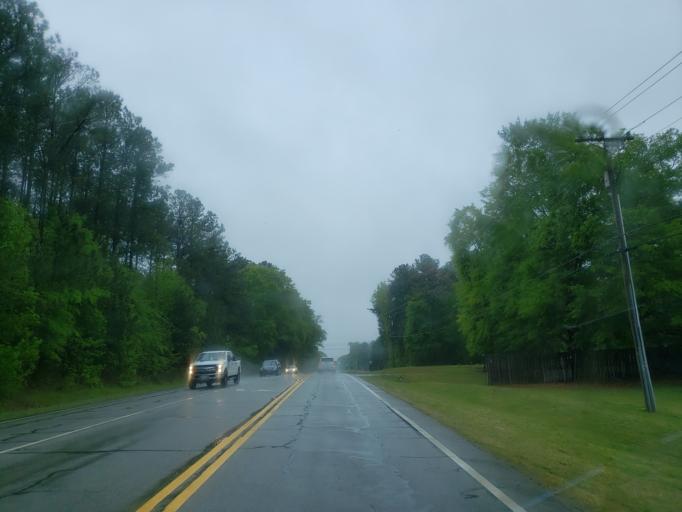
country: US
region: Georgia
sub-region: Carroll County
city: Villa Rica
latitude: 33.8114
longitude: -84.8876
